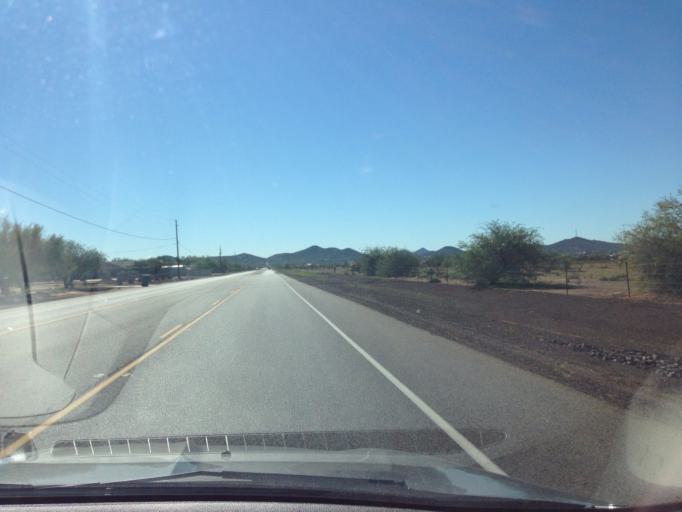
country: US
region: Arizona
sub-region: Maricopa County
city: Anthem
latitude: 33.8259
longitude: -112.0655
